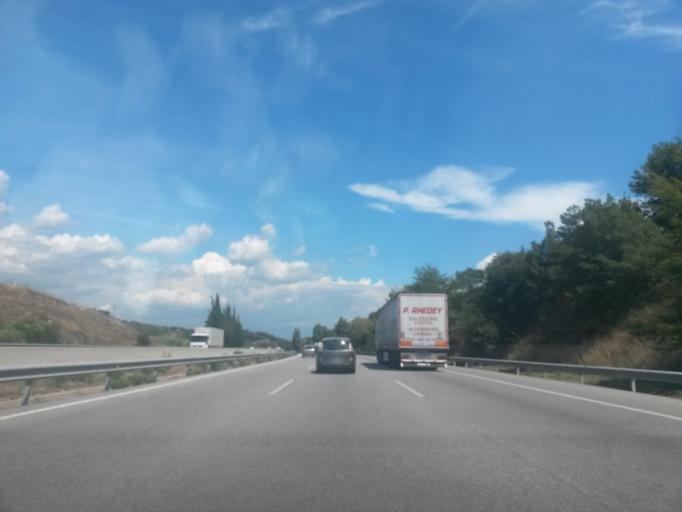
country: ES
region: Catalonia
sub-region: Provincia de Barcelona
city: Llinars del Valles
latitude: 41.6518
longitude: 2.4436
